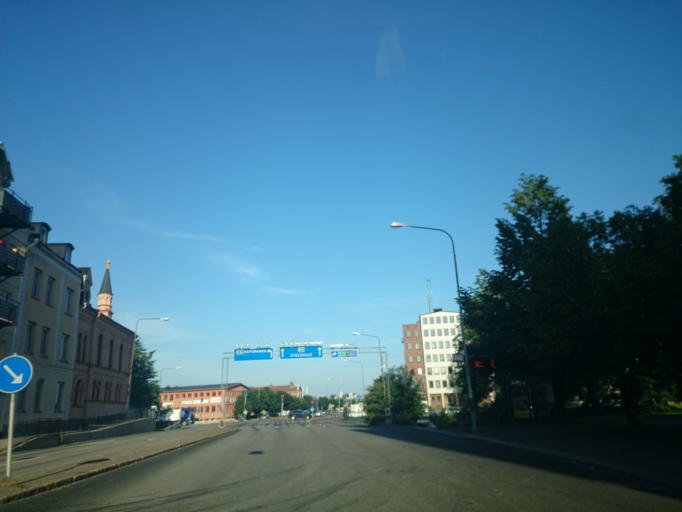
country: SE
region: Vaesternorrland
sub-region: Sundsvalls Kommun
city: Sundsvall
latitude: 62.3883
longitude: 17.3118
